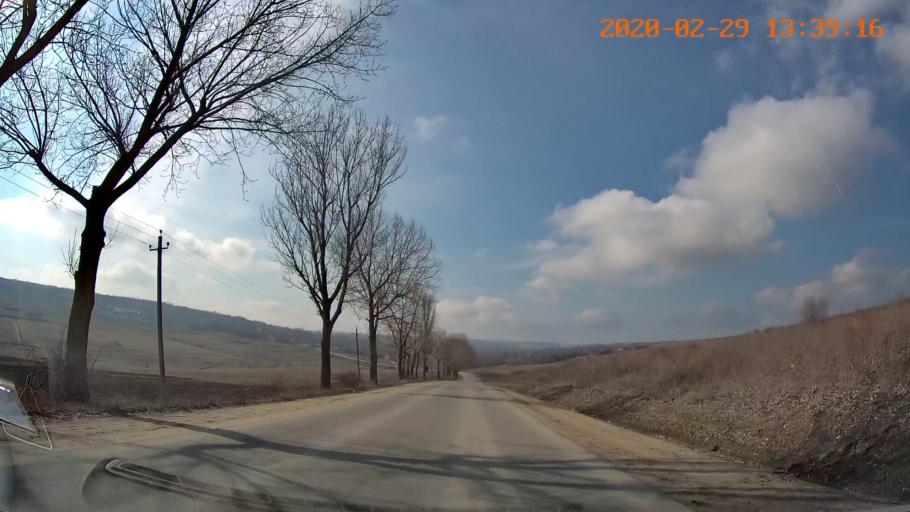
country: MD
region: Floresti
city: Leninskiy
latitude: 47.8515
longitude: 28.5842
